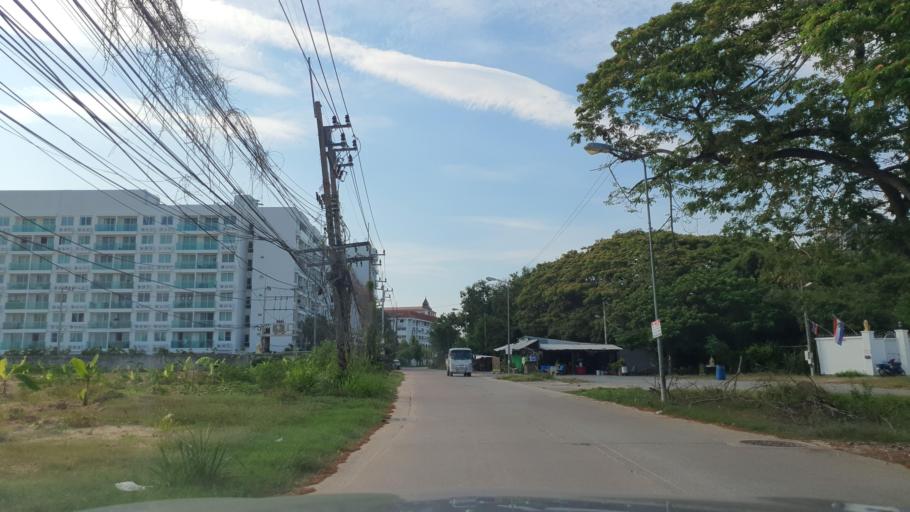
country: TH
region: Chon Buri
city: Phatthaya
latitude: 12.8868
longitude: 100.8890
